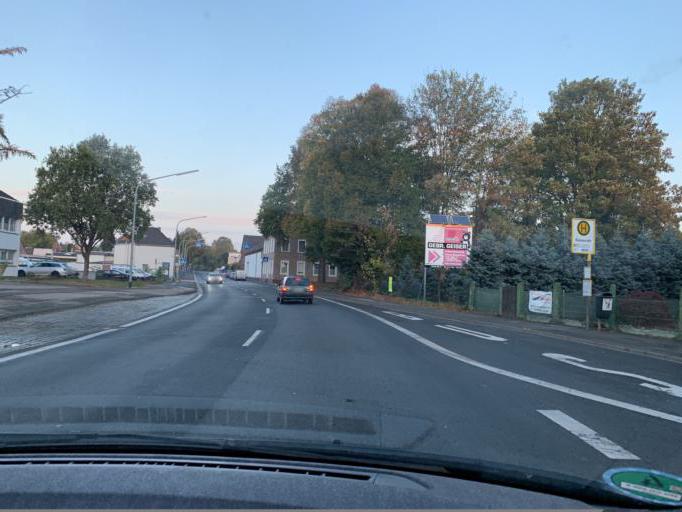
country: DE
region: North Rhine-Westphalia
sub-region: Regierungsbezirk Dusseldorf
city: Juchen
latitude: 51.1212
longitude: 6.4628
